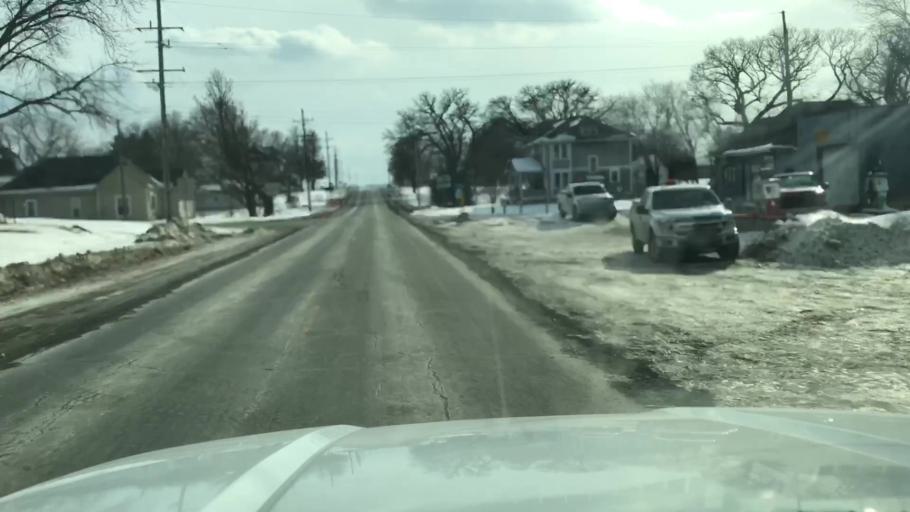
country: US
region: Missouri
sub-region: Gentry County
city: Stanberry
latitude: 40.3509
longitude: -94.6733
